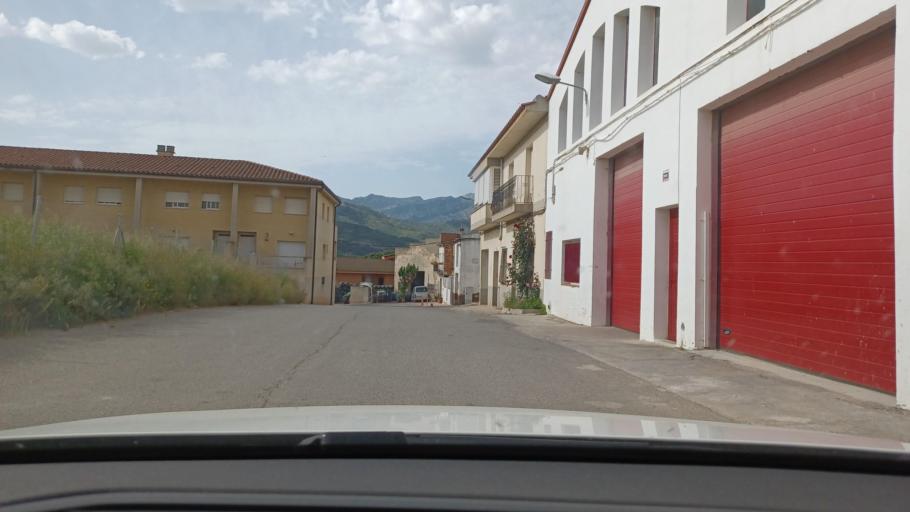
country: ES
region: Catalonia
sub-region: Provincia de Tarragona
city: Bot
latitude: 41.0089
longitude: 0.3820
